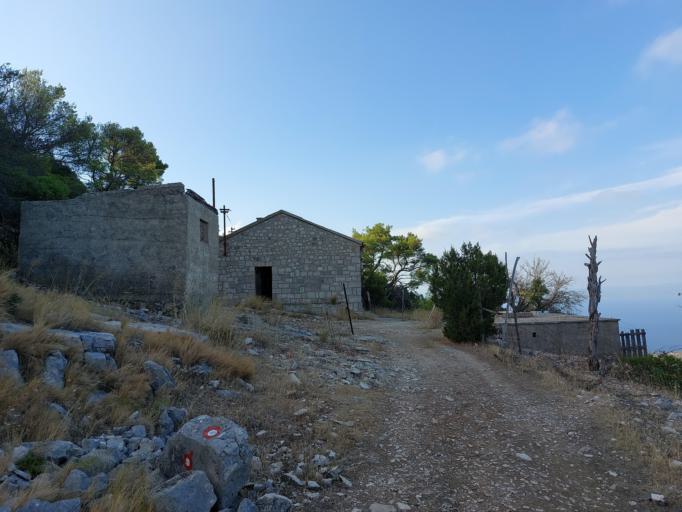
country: HR
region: Dubrovacko-Neretvanska
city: Smokvica
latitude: 42.7518
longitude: 16.8622
